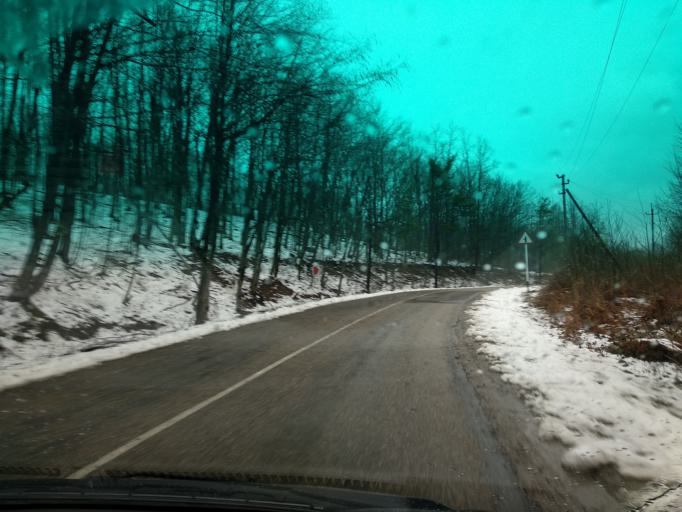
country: RU
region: Krasnodarskiy
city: Khadyzhensk
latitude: 44.2060
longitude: 39.3983
